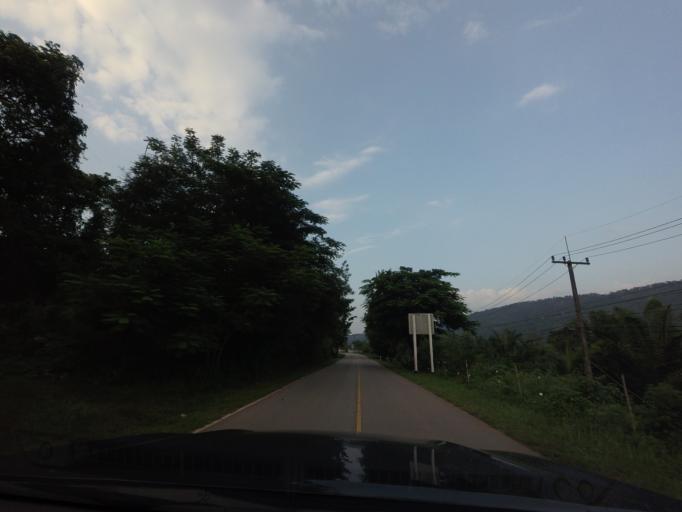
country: TH
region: Loei
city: Na Haeo
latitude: 17.4167
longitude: 101.0470
